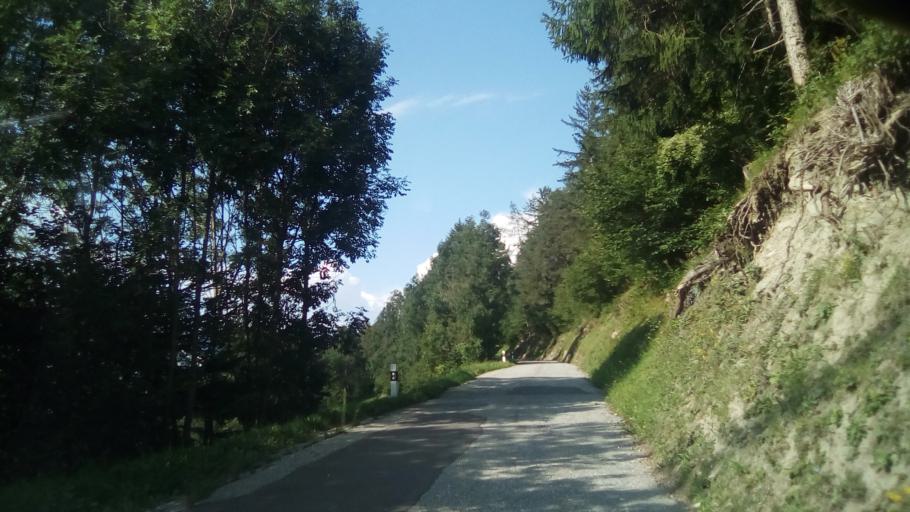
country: CH
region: Valais
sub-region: Entremont District
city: Orsieres
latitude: 46.0460
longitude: 7.1498
